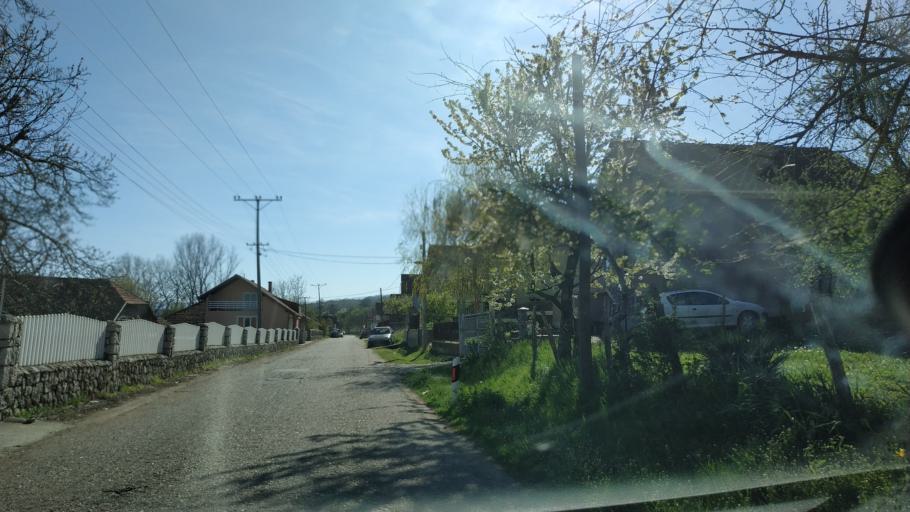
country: RS
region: Central Serbia
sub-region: Nisavski Okrug
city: Aleksinac
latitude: 43.4888
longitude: 21.6631
